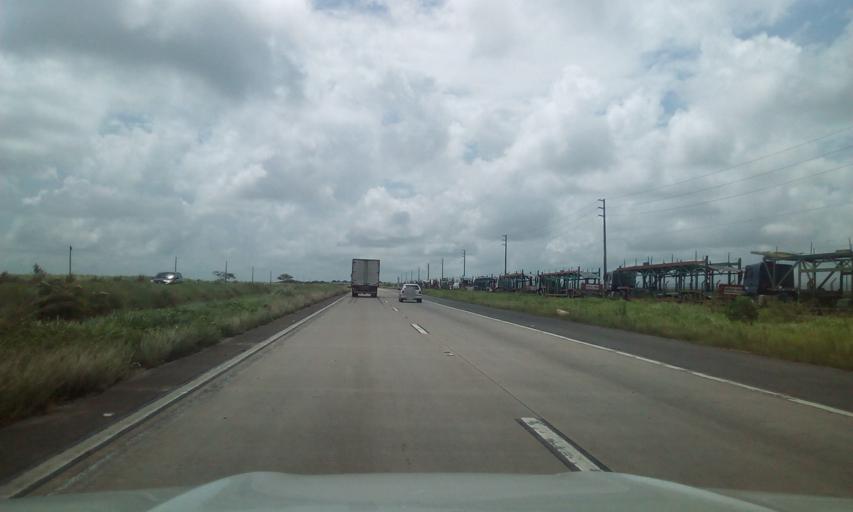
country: BR
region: Pernambuco
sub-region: Goiana
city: Goiana
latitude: -7.6225
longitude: -34.9686
